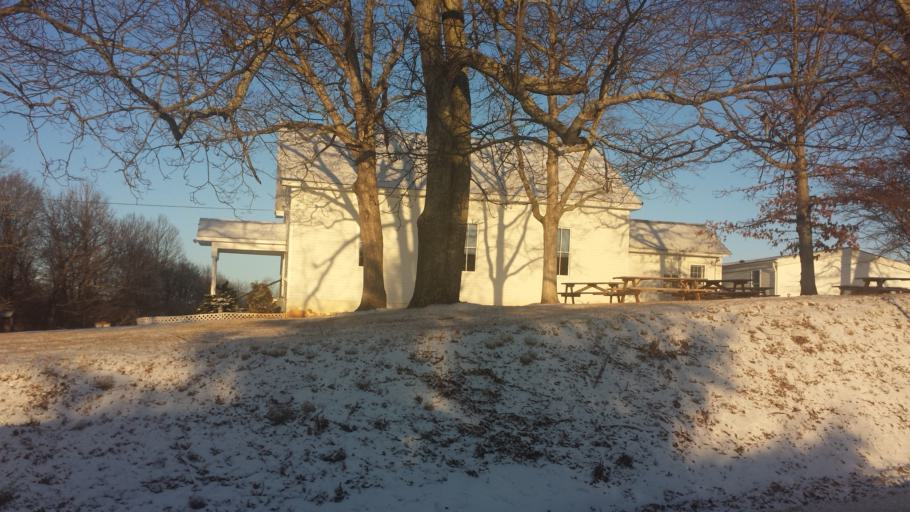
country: US
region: Virginia
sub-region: Floyd County
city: Floyd
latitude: 37.0000
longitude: -80.1796
